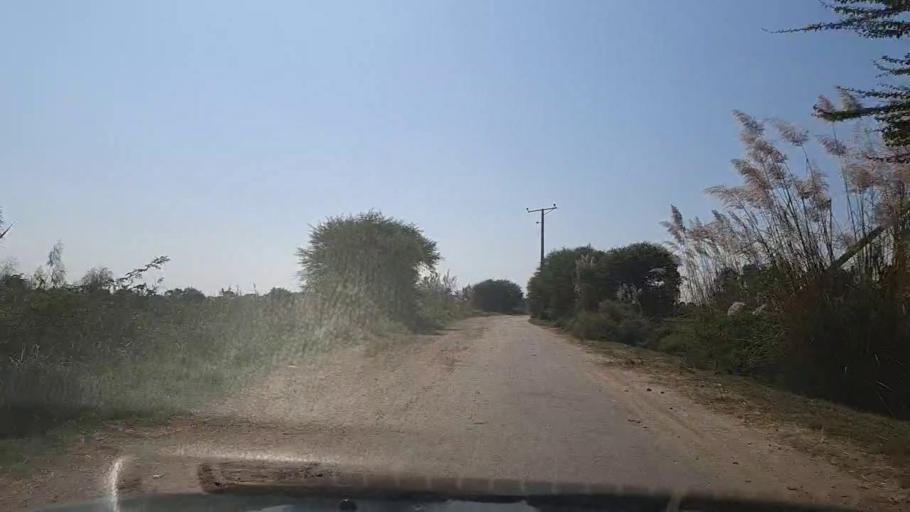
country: PK
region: Sindh
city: Mirpur Sakro
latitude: 24.6016
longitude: 67.7864
